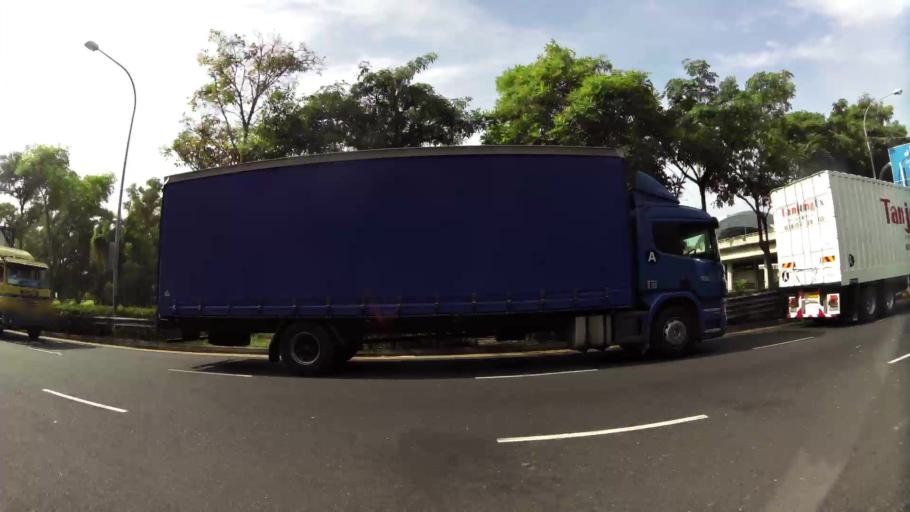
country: MY
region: Johor
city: Johor Bahru
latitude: 1.3472
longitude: 103.6374
